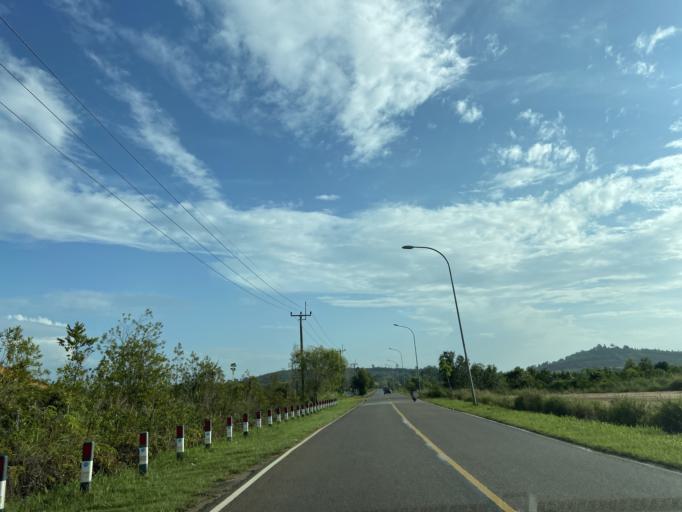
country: SG
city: Singapore
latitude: 0.9521
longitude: 104.0524
